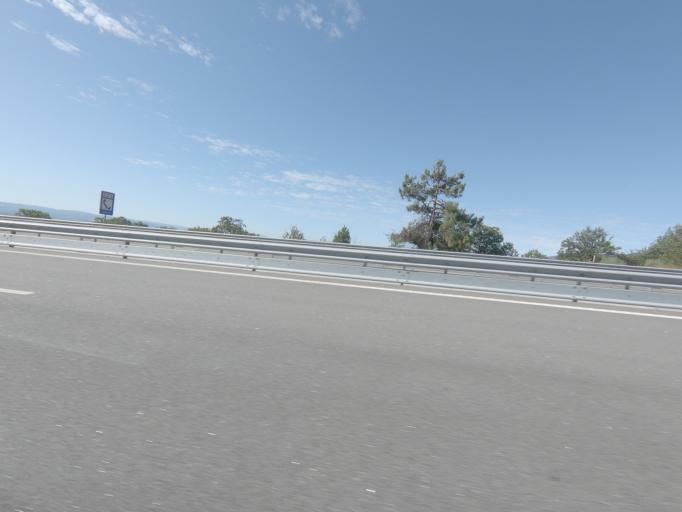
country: PT
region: Vila Real
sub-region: Santa Marta de Penaguiao
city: Santa Marta de Penaguiao
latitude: 41.2659
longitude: -7.8118
